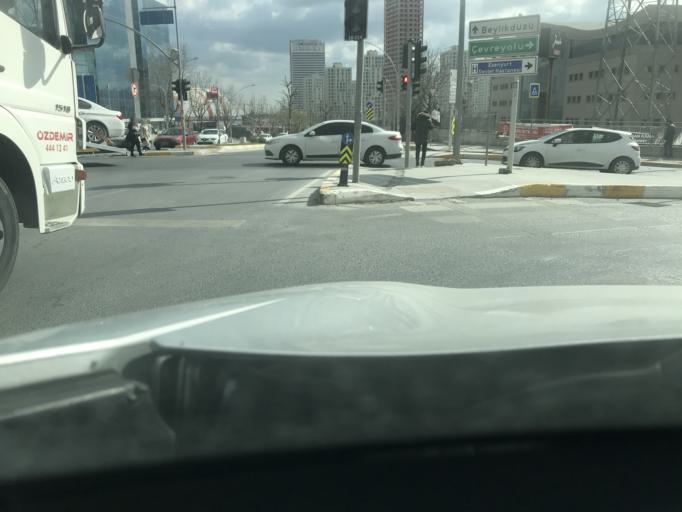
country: TR
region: Istanbul
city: Esenyurt
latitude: 41.0148
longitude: 28.6821
